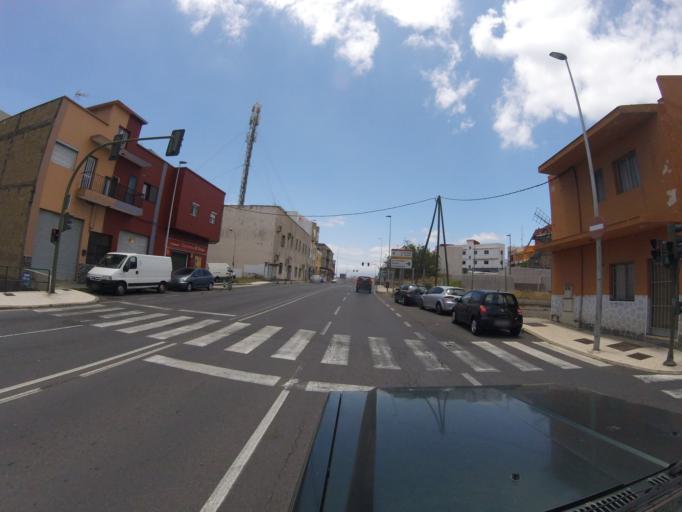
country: ES
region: Canary Islands
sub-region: Provincia de Santa Cruz de Tenerife
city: La Laguna
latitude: 28.4383
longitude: -16.3054
